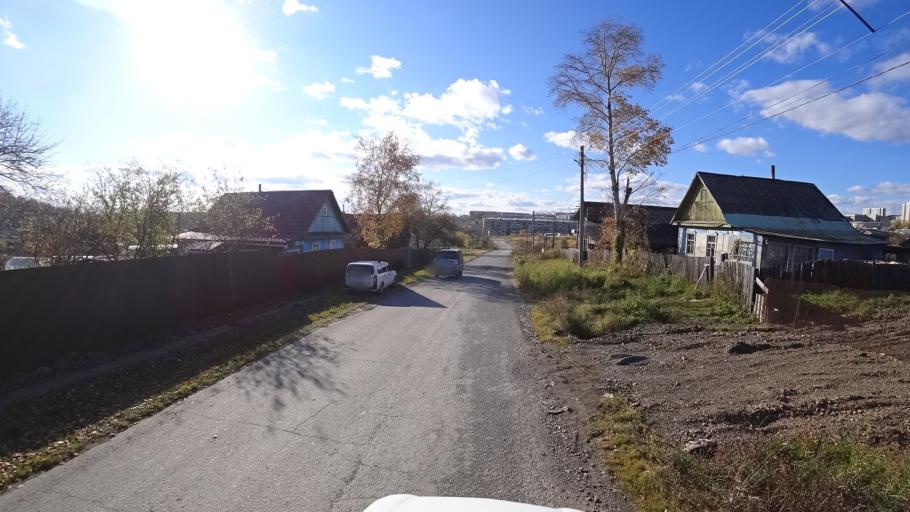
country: RU
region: Khabarovsk Krai
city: Amursk
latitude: 50.2354
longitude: 136.9172
